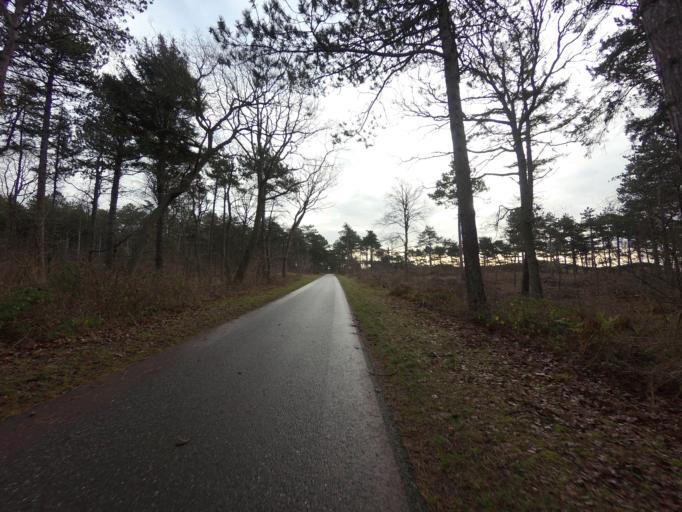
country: NL
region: North Holland
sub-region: Gemeente Texel
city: Den Burg
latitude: 53.0439
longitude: 4.7280
